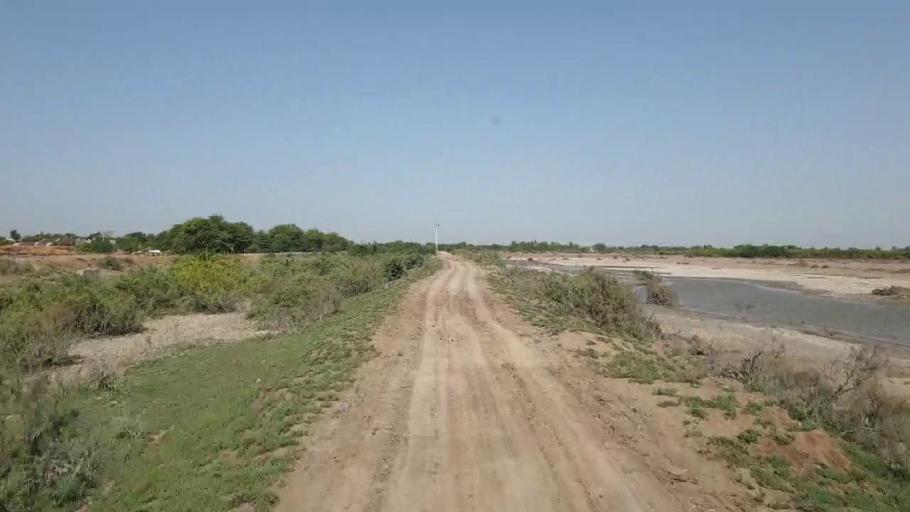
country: PK
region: Sindh
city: Tando Bago
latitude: 24.6614
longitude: 69.0683
